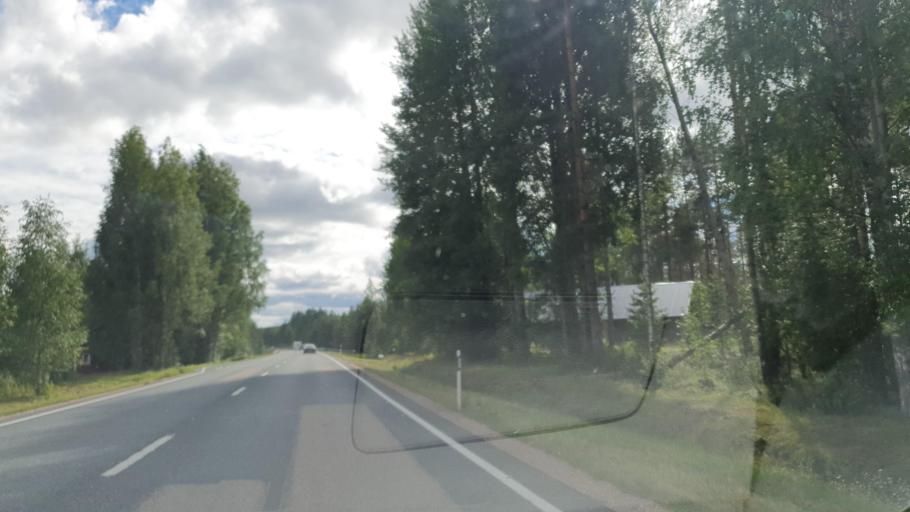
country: FI
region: Kainuu
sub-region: Kajaani
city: Kajaani
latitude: 64.1102
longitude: 27.4481
